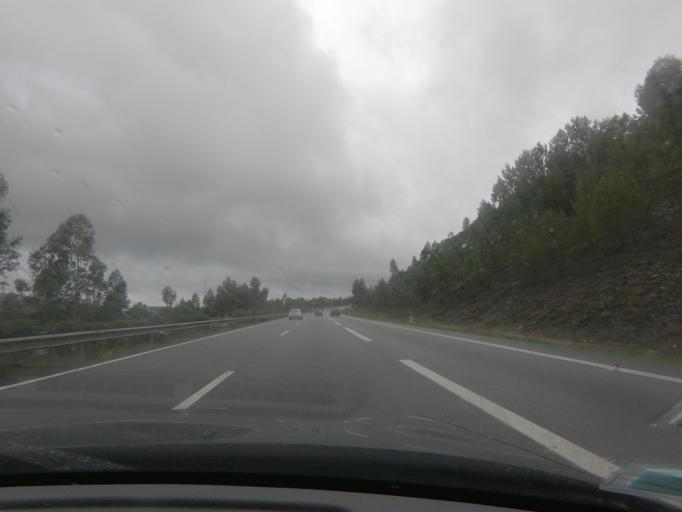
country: PT
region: Porto
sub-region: Valongo
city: Campo
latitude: 41.1879
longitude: -8.4747
